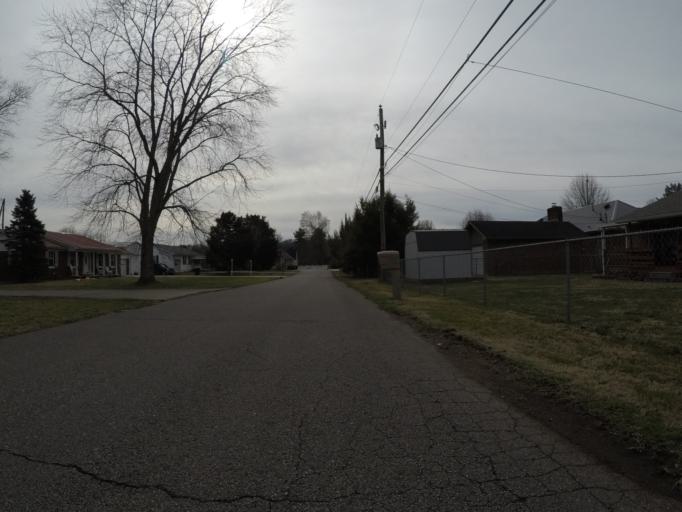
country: US
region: West Virginia
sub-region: Cabell County
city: Pea Ridge
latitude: 38.4517
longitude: -82.3414
